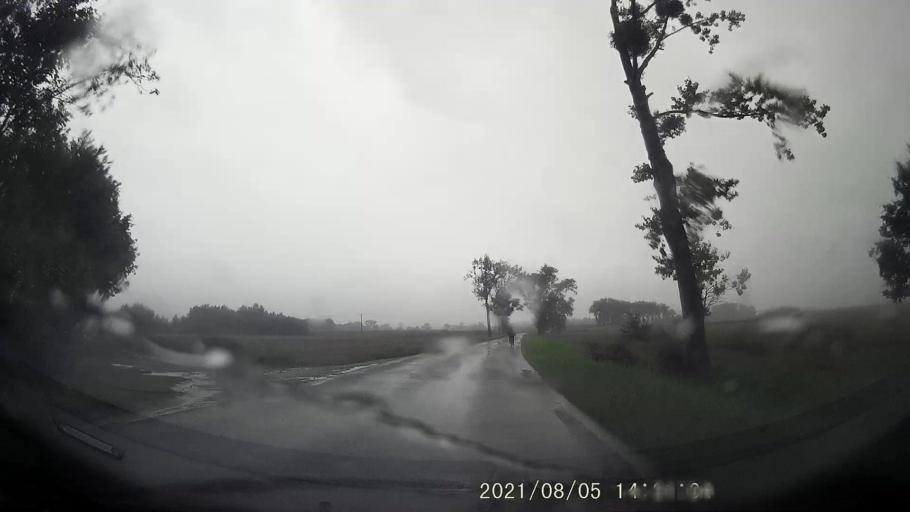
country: PL
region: Opole Voivodeship
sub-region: Powiat nyski
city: Korfantow
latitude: 50.4787
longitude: 17.5581
